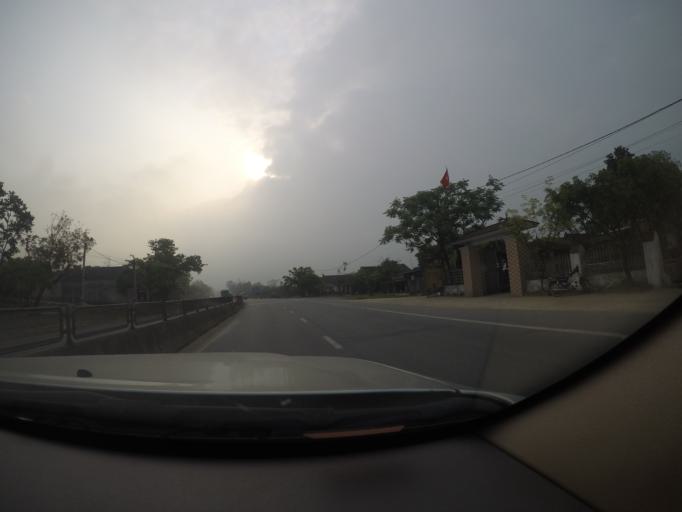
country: VN
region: Ha Tinh
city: Cam Xuyen
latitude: 18.2037
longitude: 106.1312
